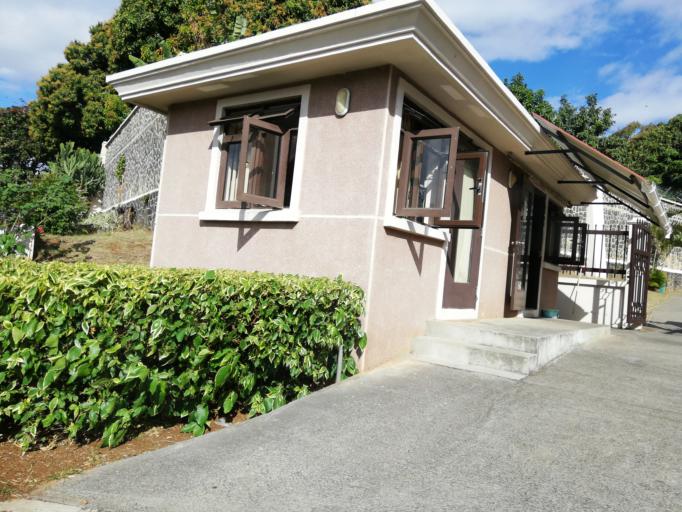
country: MU
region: Plaines Wilhems
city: Ebene
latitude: -20.2297
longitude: 57.4606
